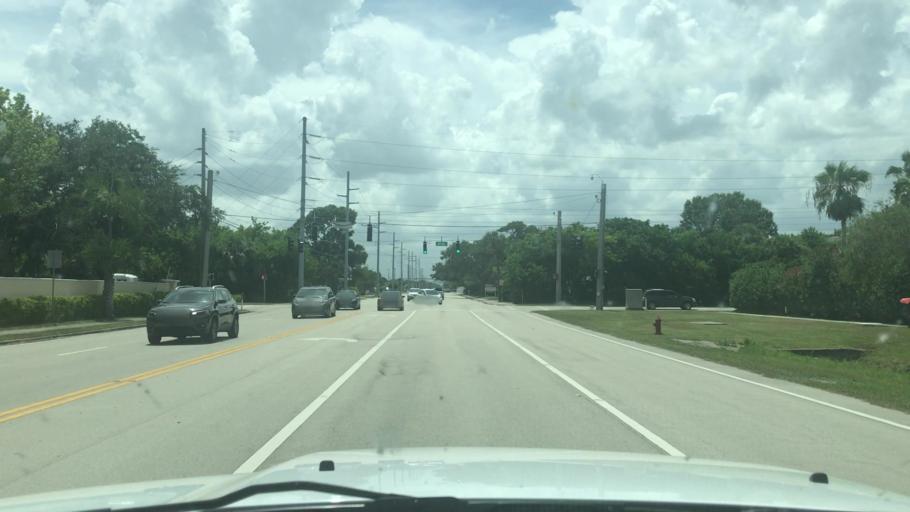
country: US
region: Florida
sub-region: Indian River County
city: Vero Beach
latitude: 27.6234
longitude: -80.3844
